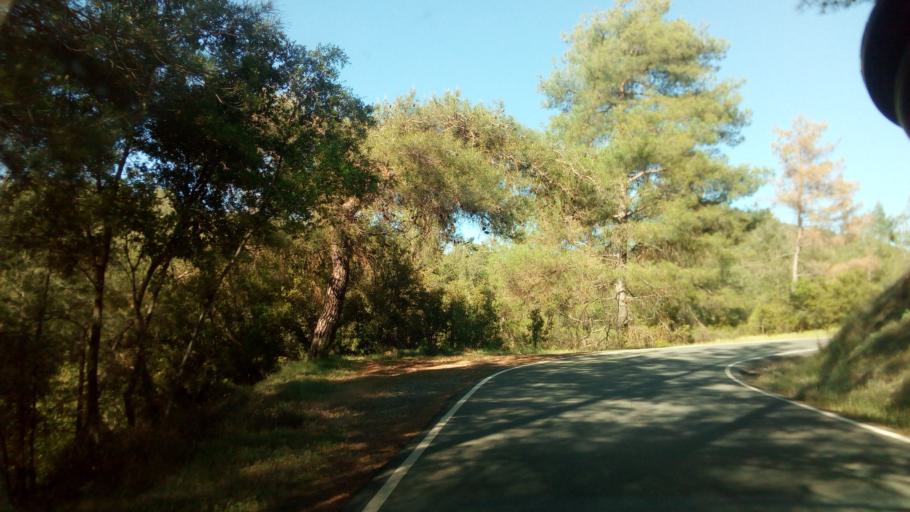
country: CY
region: Limassol
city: Pachna
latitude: 34.8883
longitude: 32.7544
